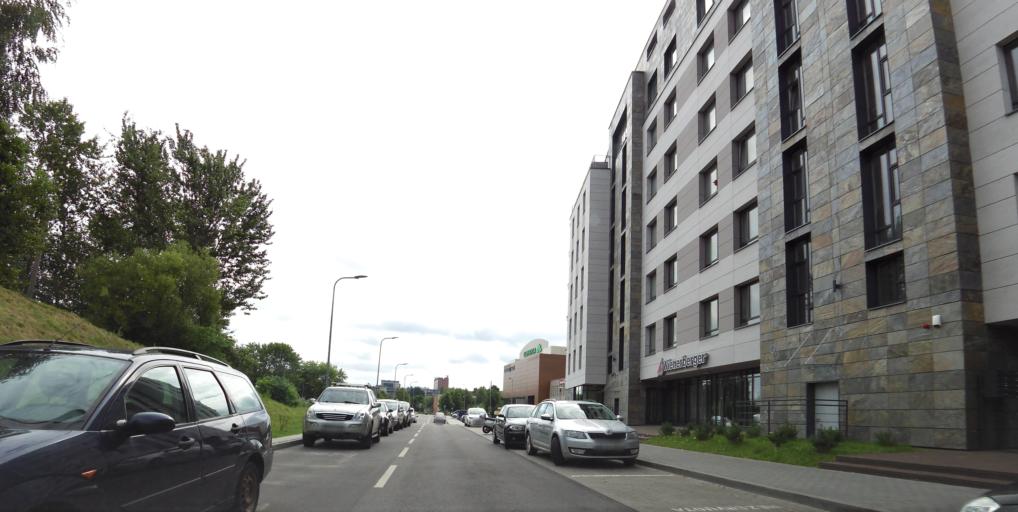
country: LT
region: Vilnius County
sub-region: Vilnius
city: Vilnius
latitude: 54.7123
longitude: 25.2748
